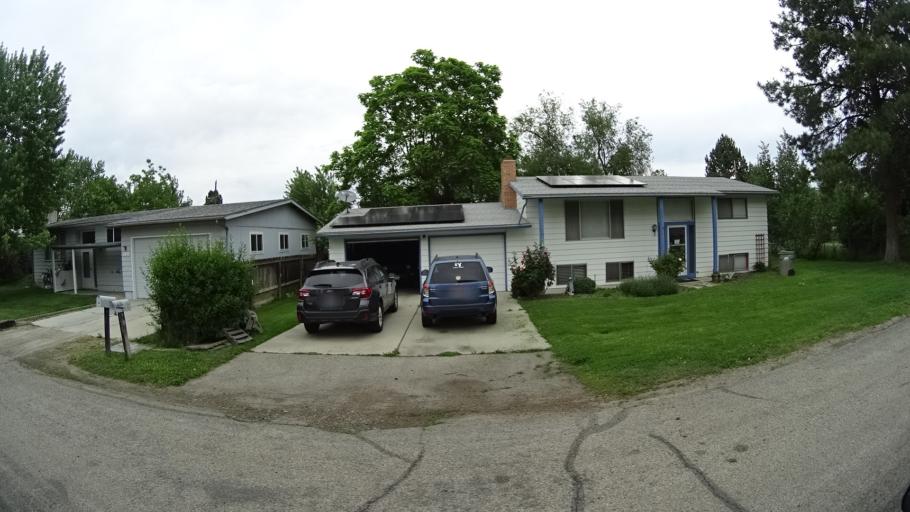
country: US
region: Idaho
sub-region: Ada County
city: Boise
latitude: 43.5826
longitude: -116.2051
